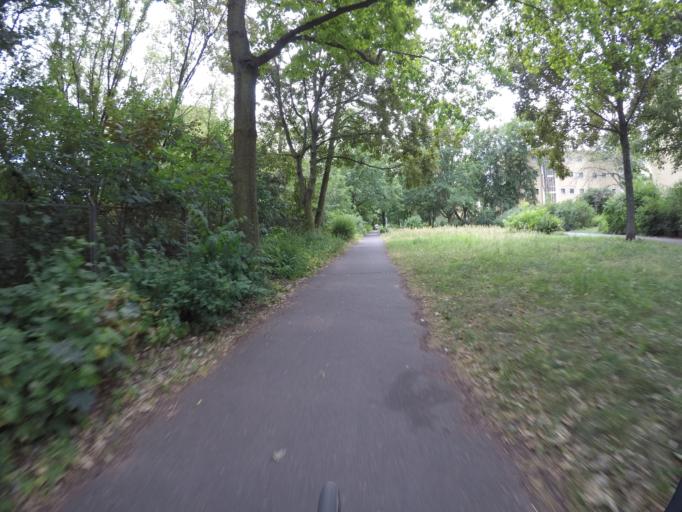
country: DE
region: Berlin
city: Reinickendorf
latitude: 52.5656
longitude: 13.3465
